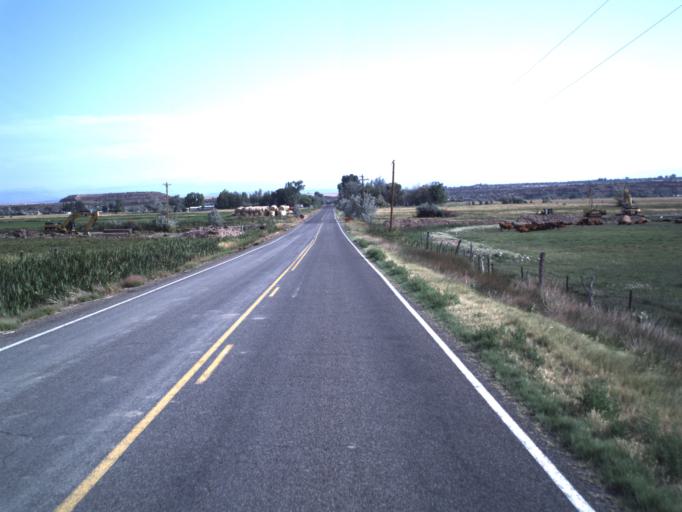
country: US
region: Utah
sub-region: Duchesne County
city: Duchesne
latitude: 40.2707
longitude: -110.2186
